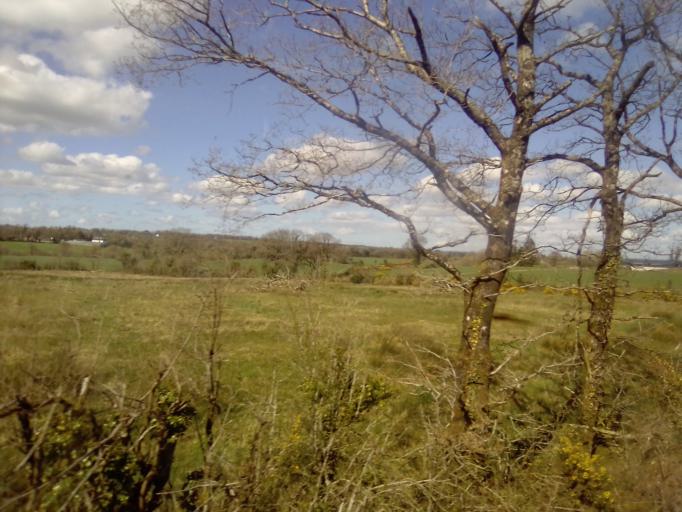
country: IE
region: Munster
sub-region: County Cork
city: Millstreet
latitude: 52.0857
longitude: -9.0191
